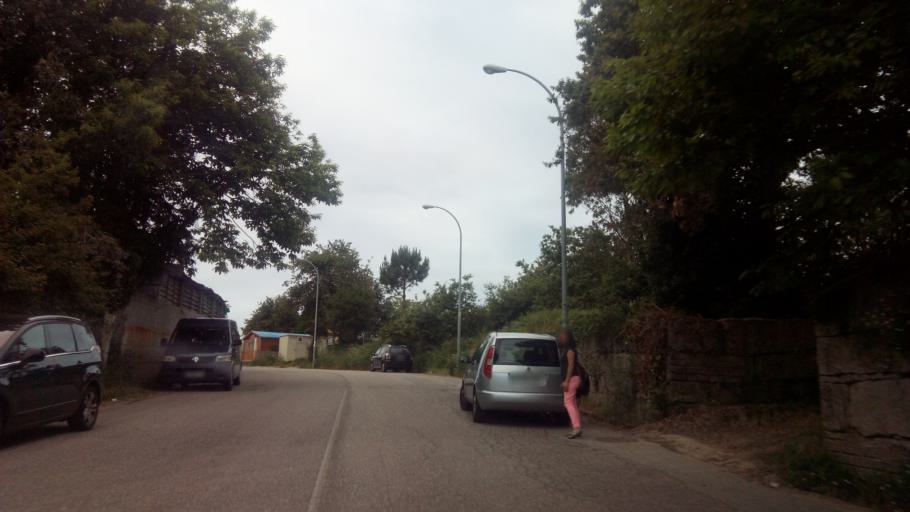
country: ES
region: Galicia
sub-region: Provincia de Pontevedra
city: Nigran
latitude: 42.1212
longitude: -8.8013
